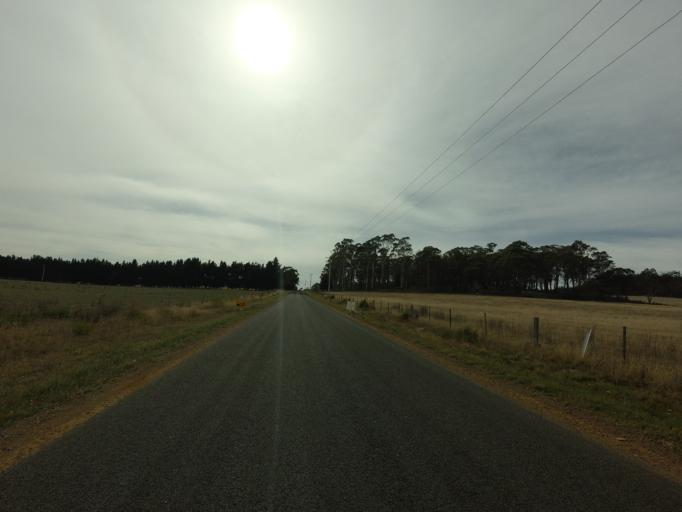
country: AU
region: Tasmania
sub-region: Sorell
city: Sorell
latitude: -42.4278
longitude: 147.4766
